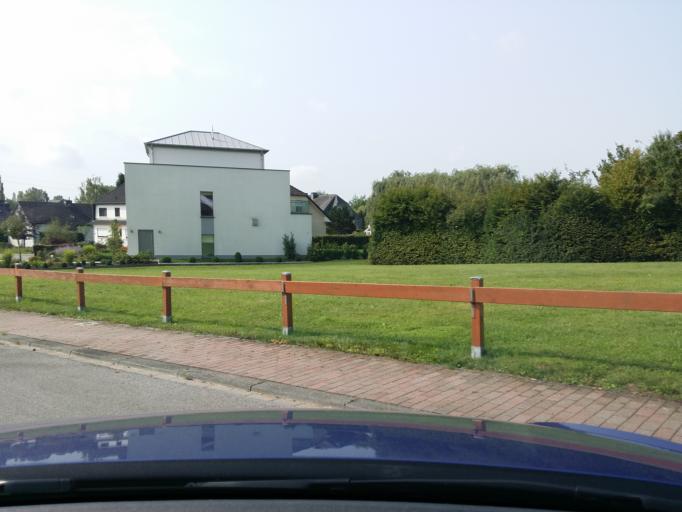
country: LU
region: Luxembourg
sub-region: Canton de Luxembourg
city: Bertrange
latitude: 49.6068
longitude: 6.0500
